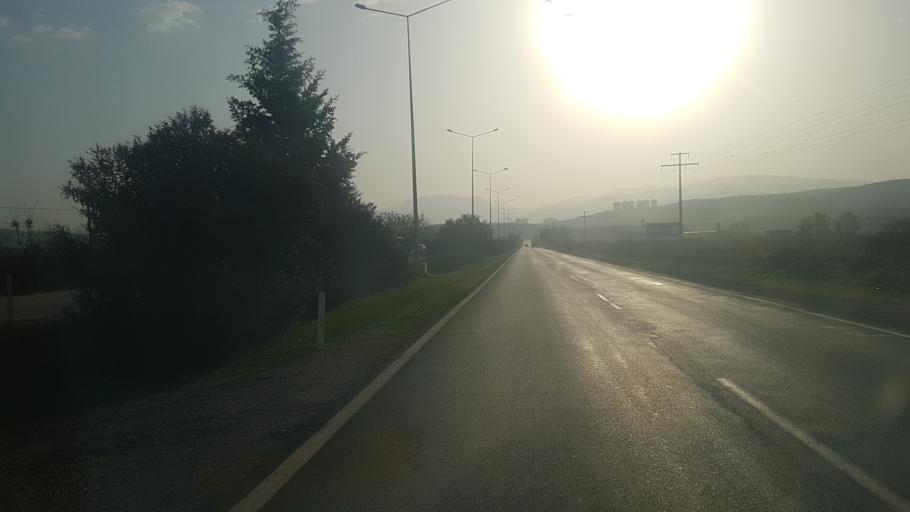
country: TR
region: Osmaniye
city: Toprakkale
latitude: 37.0543
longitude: 36.1370
